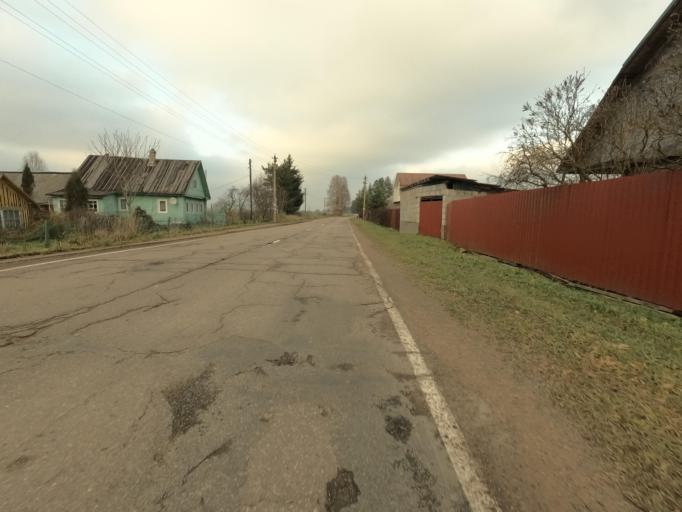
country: RU
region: Leningrad
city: Mga
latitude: 59.7755
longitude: 31.0243
